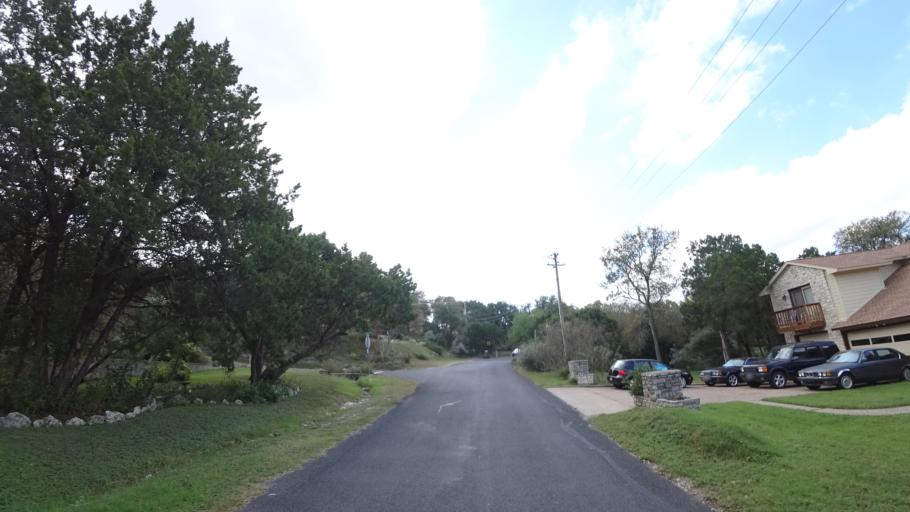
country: US
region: Texas
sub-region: Williamson County
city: Jollyville
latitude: 30.4202
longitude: -97.7831
